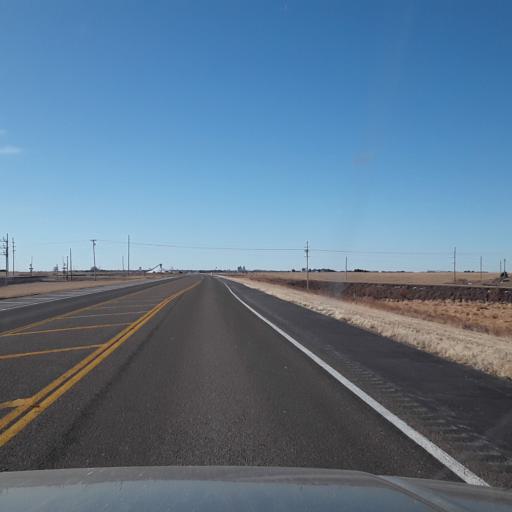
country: US
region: Nebraska
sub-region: Kearney County
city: Minden
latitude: 40.5250
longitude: -98.8918
